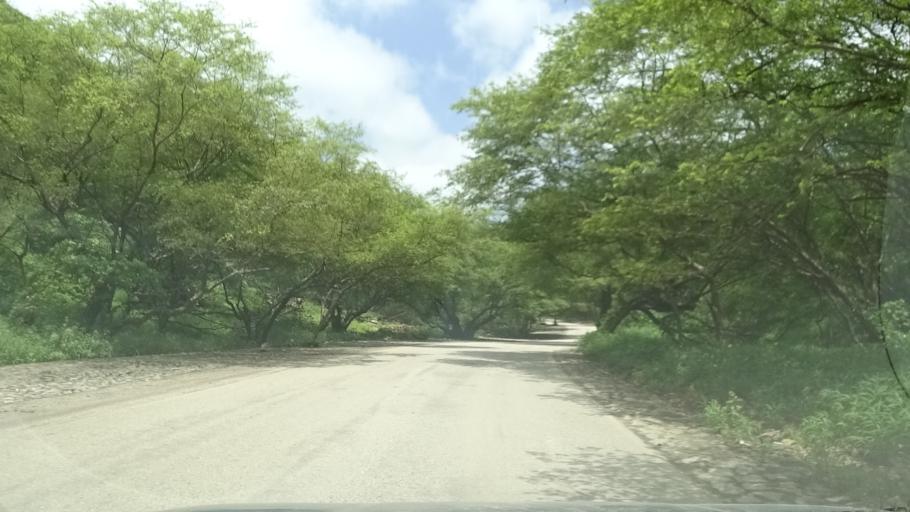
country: OM
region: Zufar
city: Salalah
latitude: 17.1705
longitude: 54.1673
